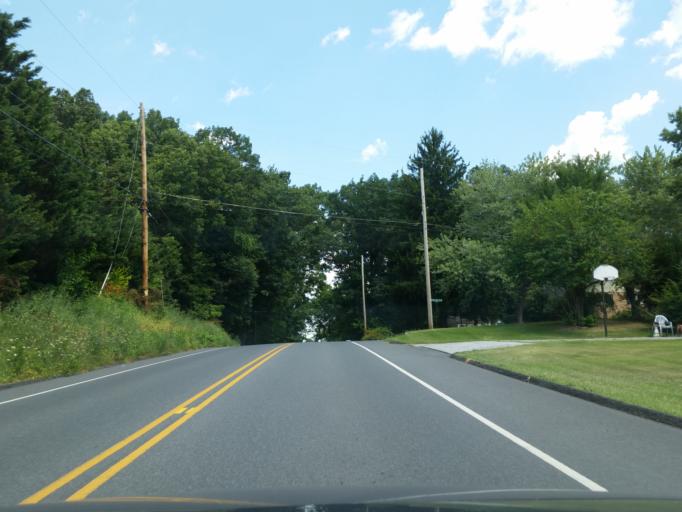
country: US
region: Pennsylvania
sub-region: Lebanon County
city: Annville
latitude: 40.3403
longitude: -76.5175
